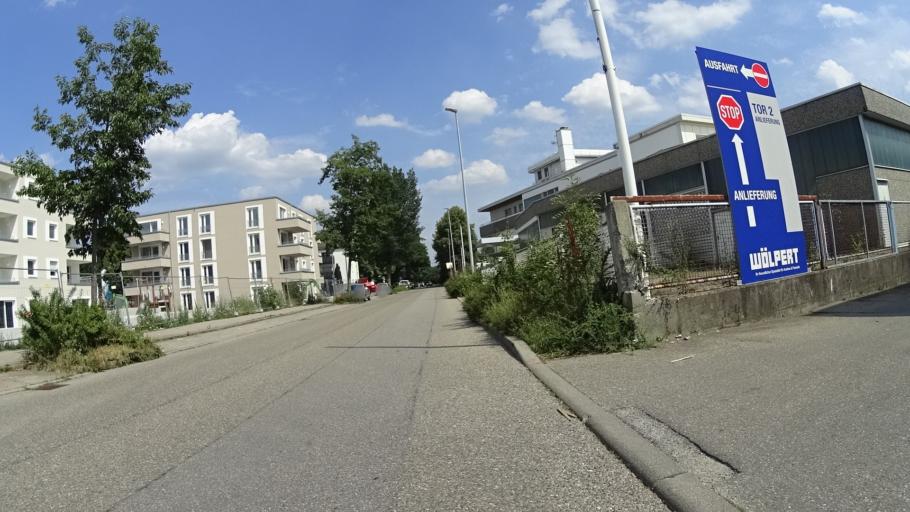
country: DE
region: Baden-Wuerttemberg
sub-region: Regierungsbezirk Stuttgart
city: Goeppingen
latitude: 48.6932
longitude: 9.6728
